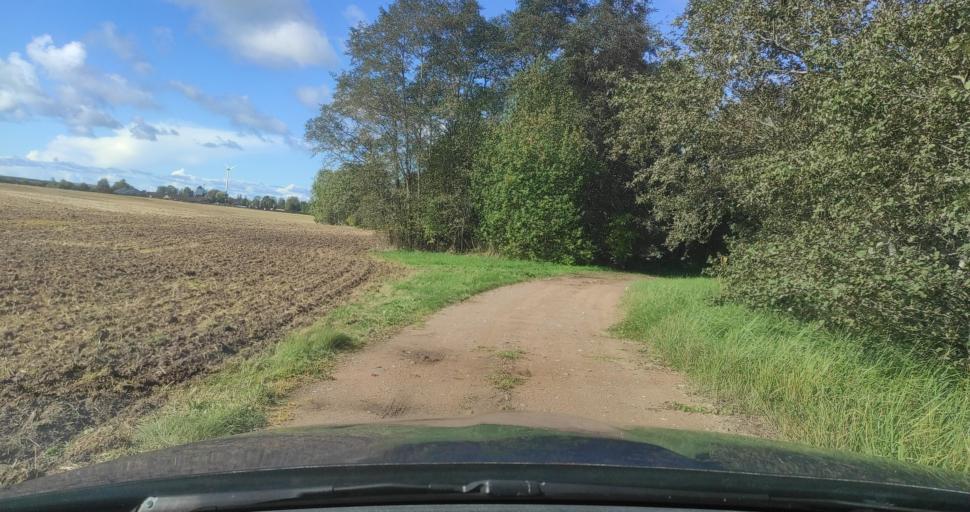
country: LV
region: Ventspils Rajons
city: Piltene
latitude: 57.2689
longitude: 21.6036
